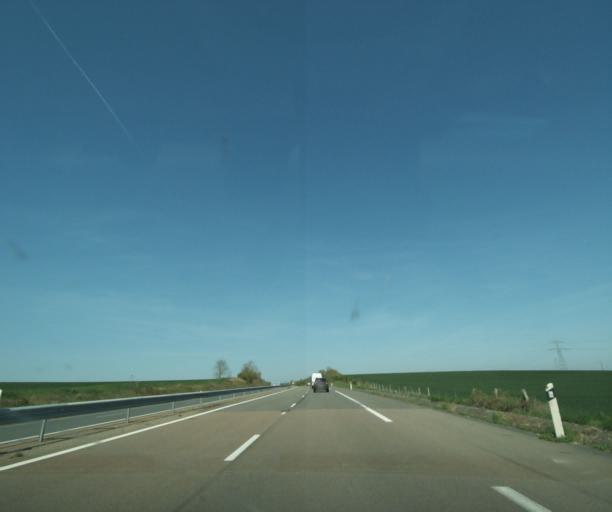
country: FR
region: Bourgogne
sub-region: Departement de la Nievre
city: La Charite-sur-Loire
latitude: 47.1677
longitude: 3.0499
